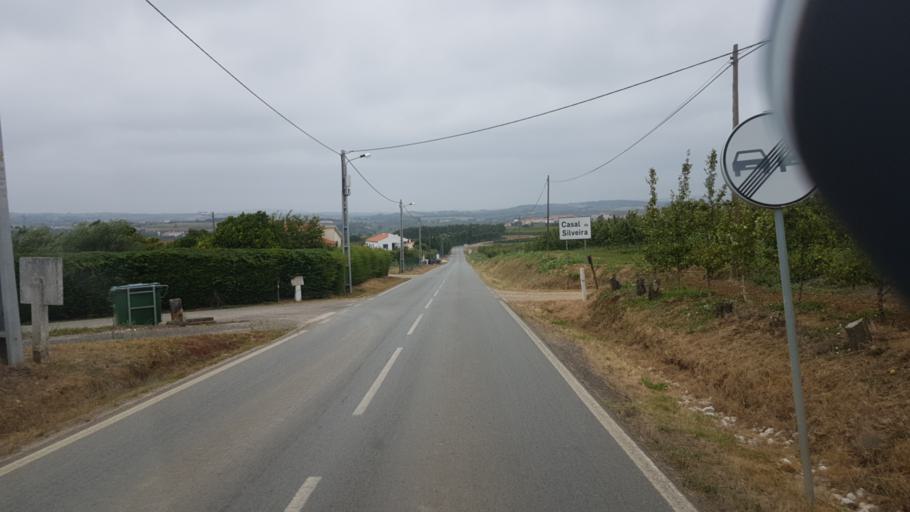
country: PT
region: Leiria
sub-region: Bombarral
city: Bombarral
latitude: 39.2761
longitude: -9.1783
